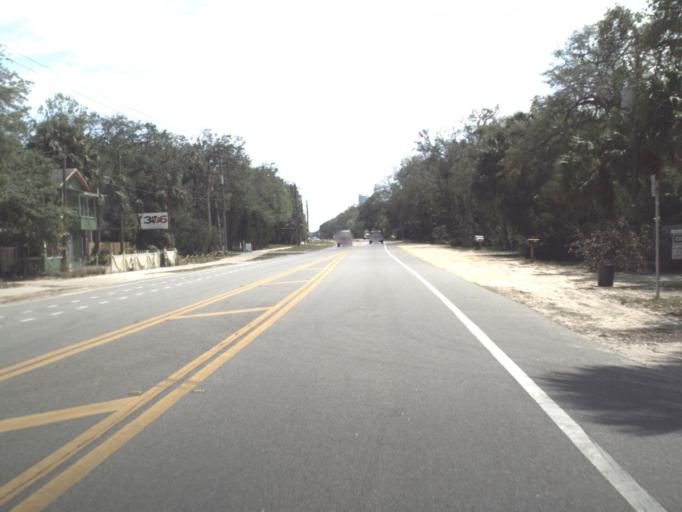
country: US
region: Florida
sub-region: Flagler County
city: Palm Coast
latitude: 29.6189
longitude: -81.2041
